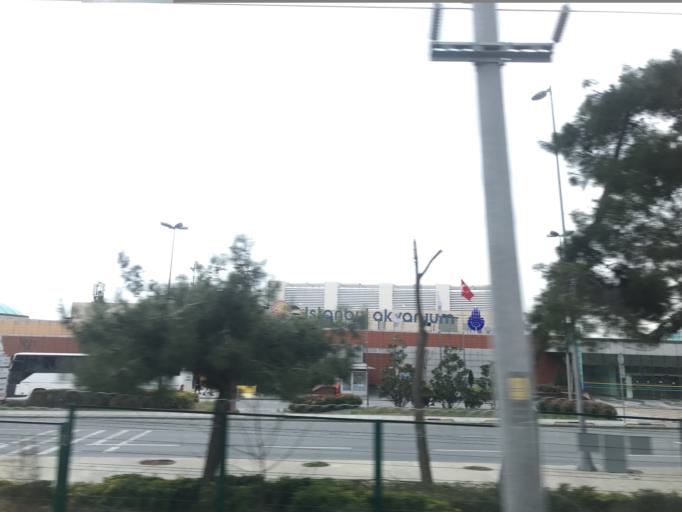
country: TR
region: Istanbul
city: Bahcelievler
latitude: 40.9651
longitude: 28.7998
